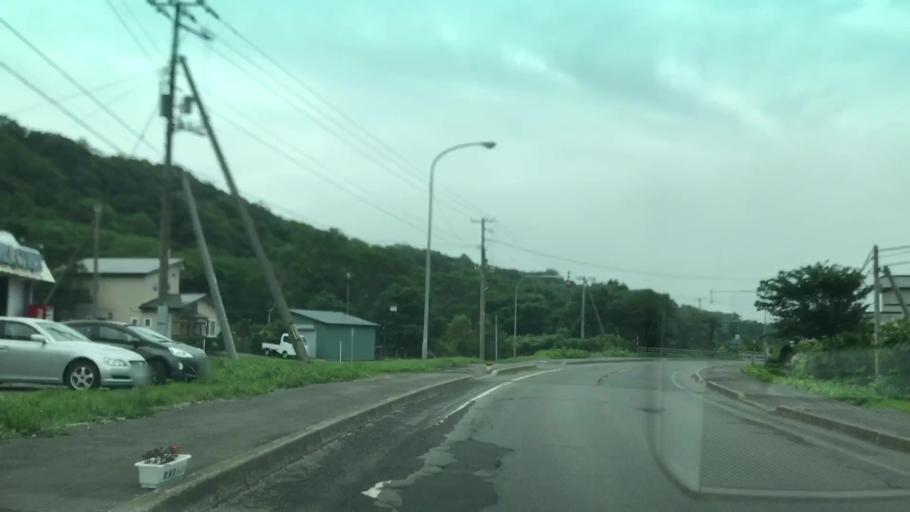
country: JP
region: Hokkaido
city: Iwanai
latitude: 42.7734
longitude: 140.3050
